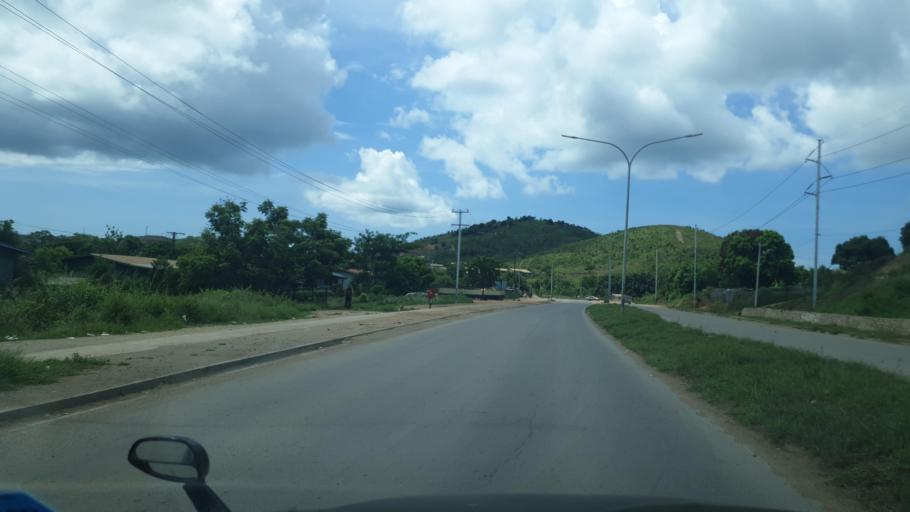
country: PG
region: National Capital
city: Port Moresby
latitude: -9.3872
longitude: 147.1544
